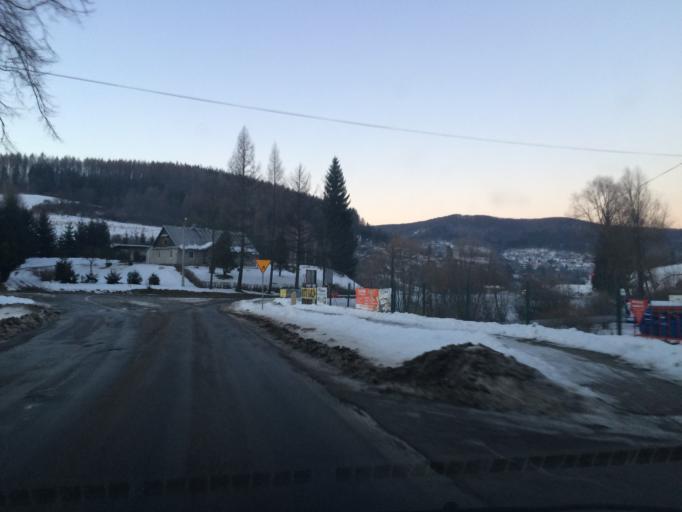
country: PL
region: Subcarpathian Voivodeship
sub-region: Powiat bieszczadzki
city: Ustrzyki Dolne
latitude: 49.4219
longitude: 22.5760
